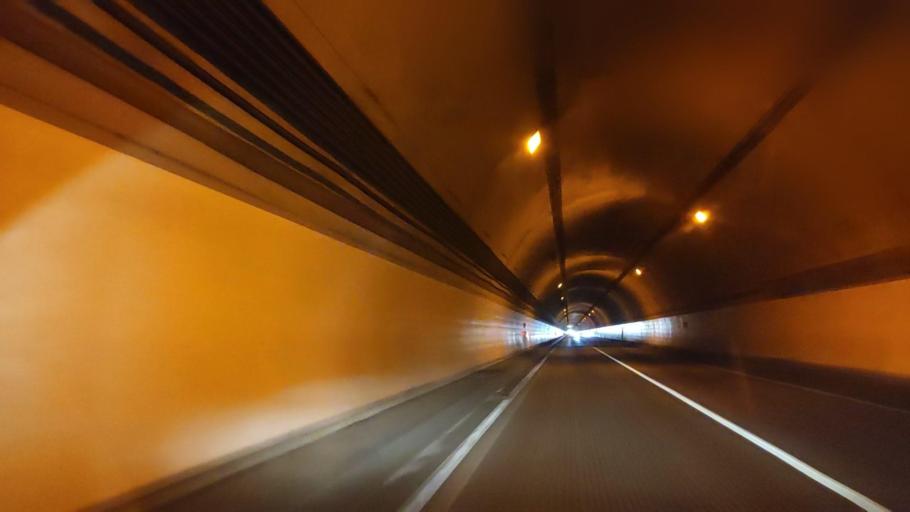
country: JP
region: Hokkaido
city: Rumoi
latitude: 43.8210
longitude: 141.4526
